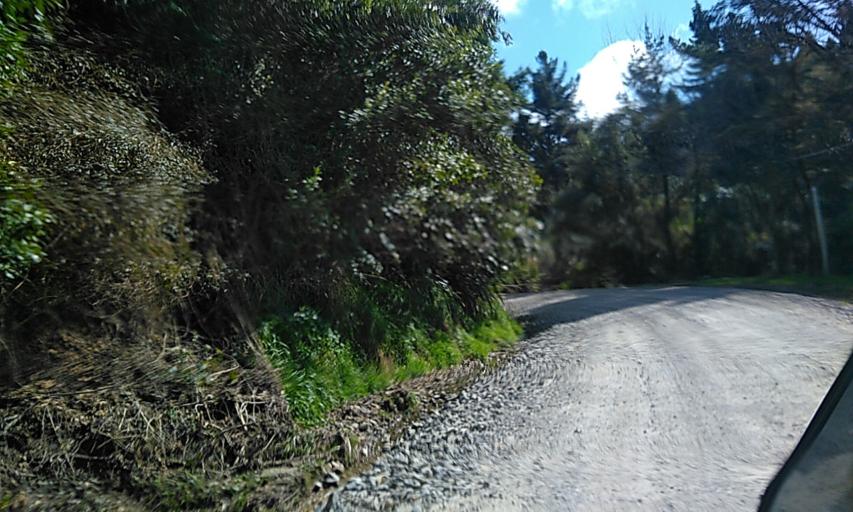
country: NZ
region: Gisborne
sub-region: Gisborne District
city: Gisborne
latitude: -38.2127
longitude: 178.0661
